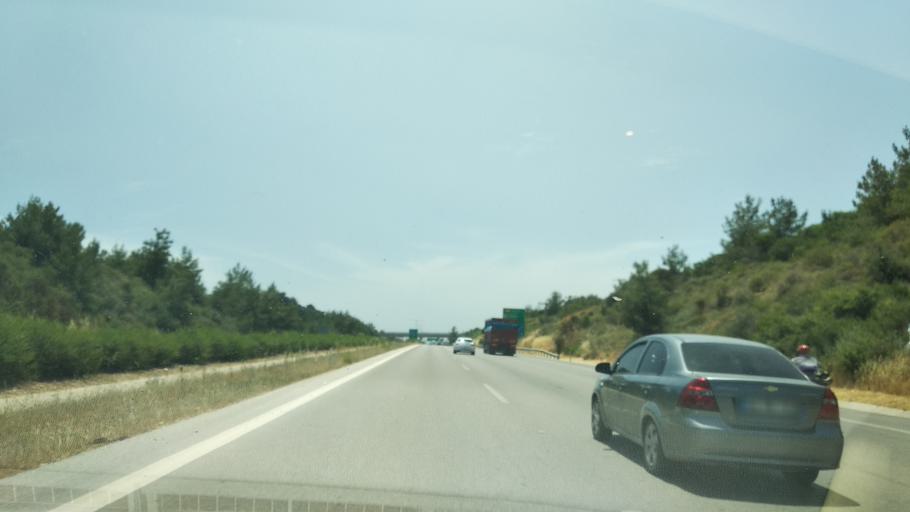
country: TR
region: Mersin
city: Mezitli
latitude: 36.7763
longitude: 34.4884
